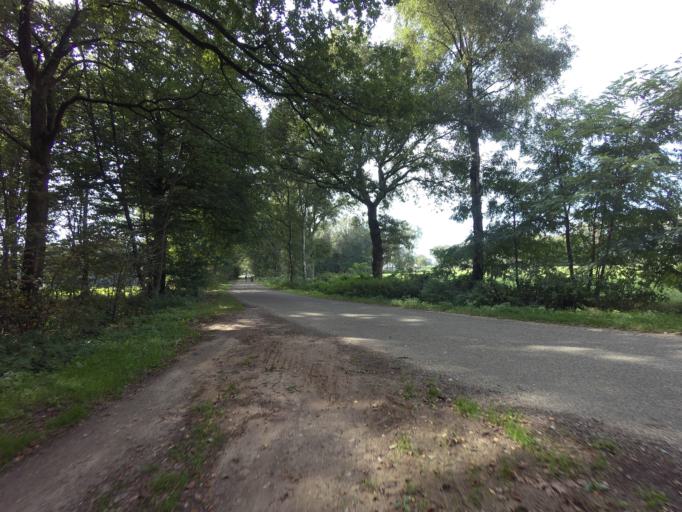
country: NL
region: Overijssel
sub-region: Gemeente Hof van Twente
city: Markelo
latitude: 52.2747
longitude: 6.4669
